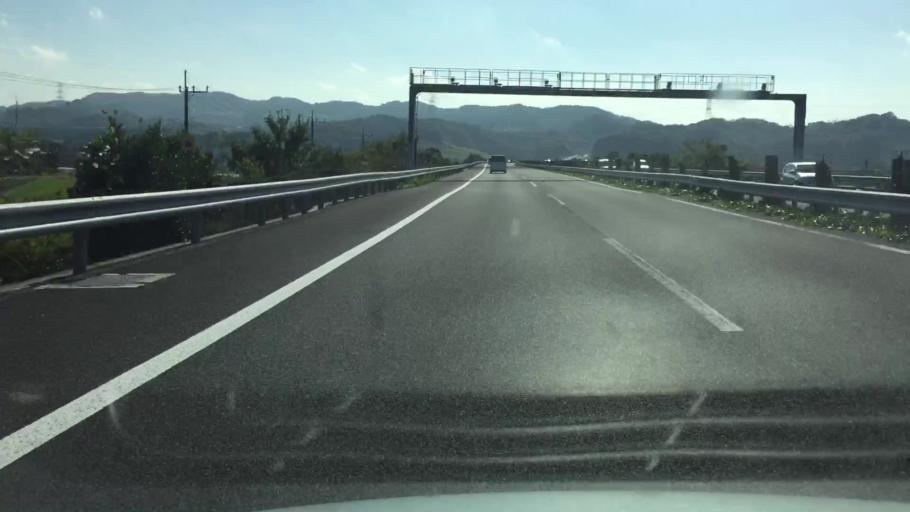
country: JP
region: Tochigi
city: Mooka
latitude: 36.3895
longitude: 140.0193
